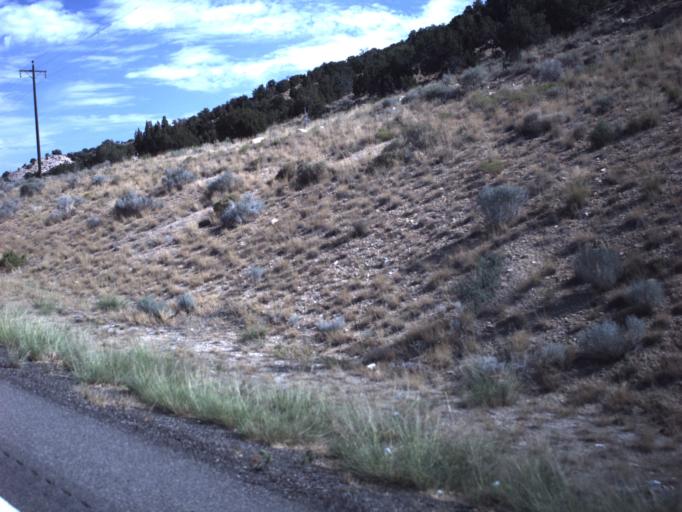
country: US
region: Utah
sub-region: Sanpete County
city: Gunnison
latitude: 39.3524
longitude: -111.9293
